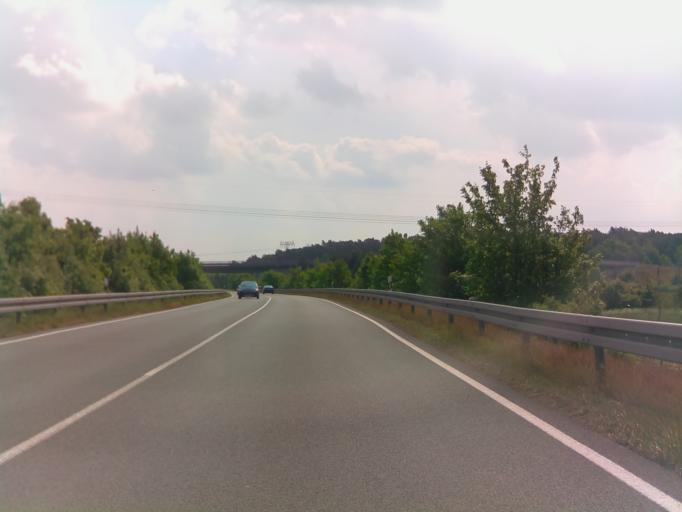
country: DE
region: Saxony-Anhalt
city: Stendal
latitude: 52.5742
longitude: 11.8380
